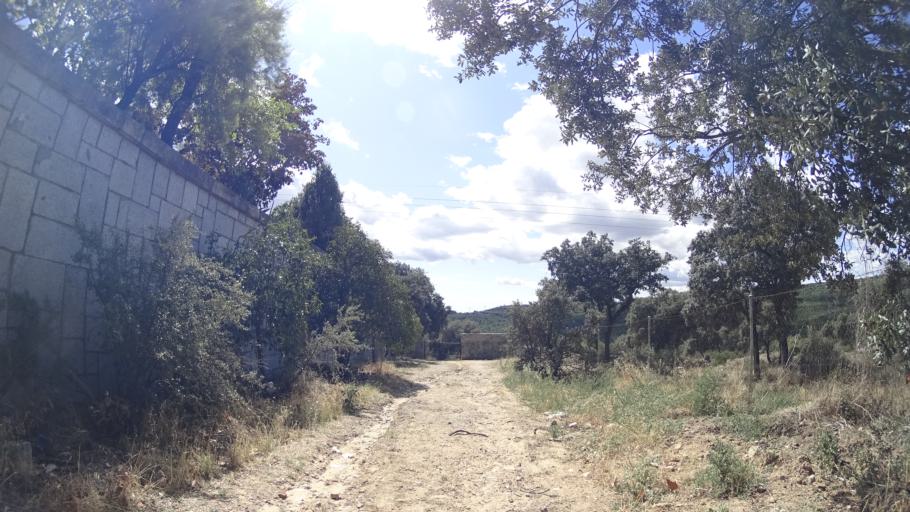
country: ES
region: Madrid
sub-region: Provincia de Madrid
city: Torrelodones
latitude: 40.5702
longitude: -3.9548
